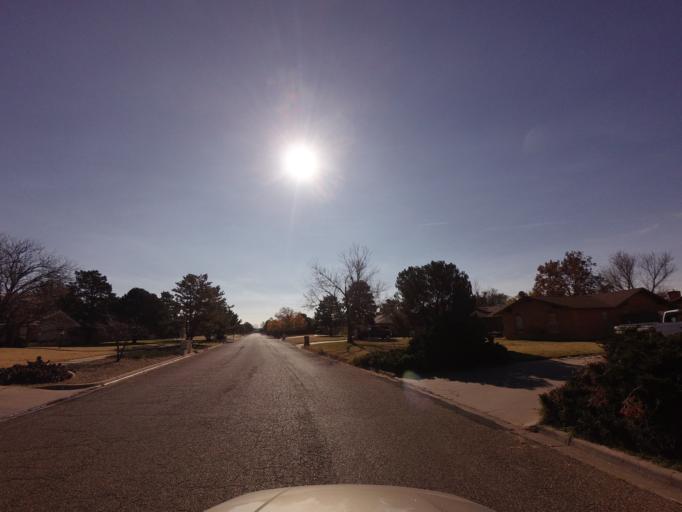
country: US
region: New Mexico
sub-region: Curry County
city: Clovis
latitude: 34.4175
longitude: -103.1860
